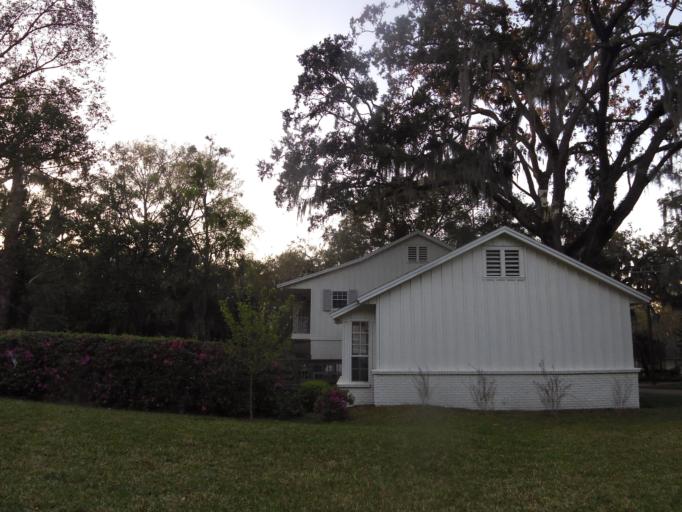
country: US
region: Florida
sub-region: Duval County
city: Jacksonville
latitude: 30.2710
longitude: -81.7109
